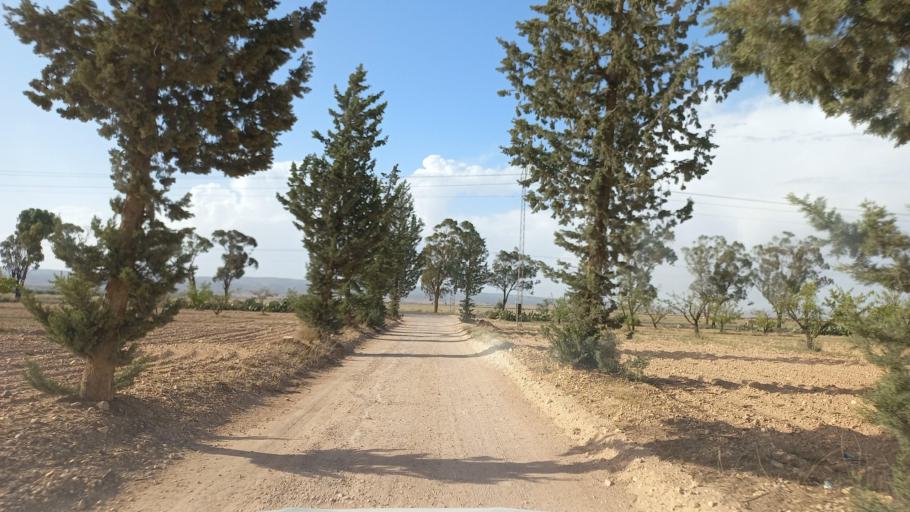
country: TN
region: Al Qasrayn
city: Kasserine
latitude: 35.2312
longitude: 8.9662
